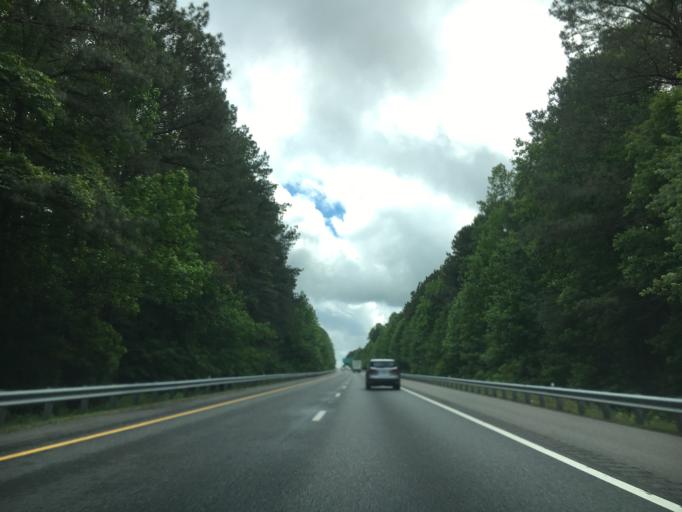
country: US
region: Virginia
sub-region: Mecklenburg County
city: South Hill
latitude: 36.7224
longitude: -78.1097
